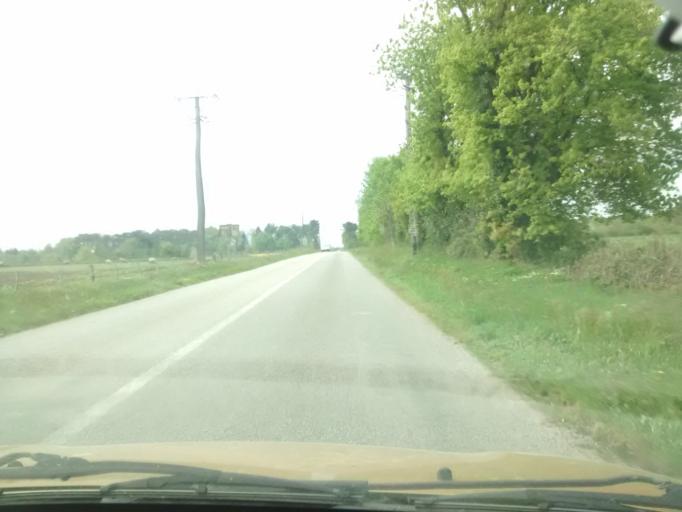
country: FR
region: Brittany
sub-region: Departement du Morbihan
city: Questembert
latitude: 47.6602
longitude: -2.4755
